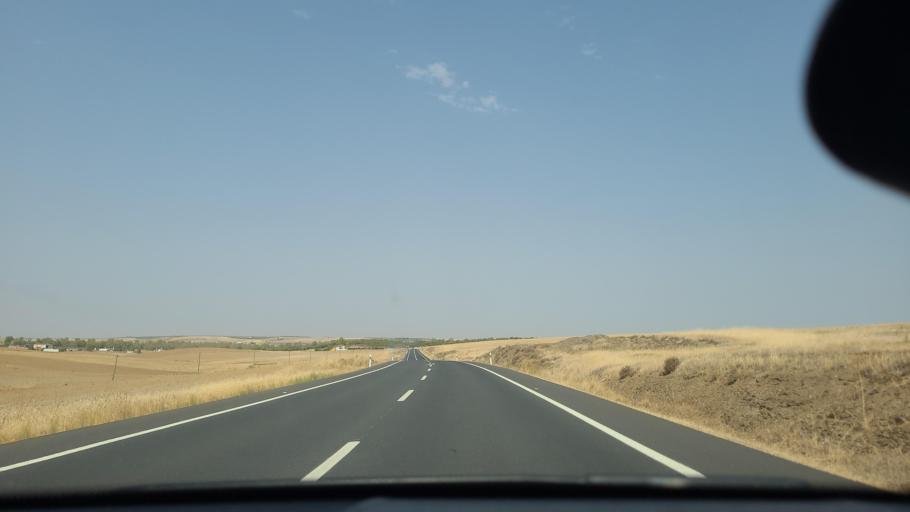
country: ES
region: Extremadura
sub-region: Provincia de Badajoz
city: Berlanga
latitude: 38.2708
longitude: -5.7952
